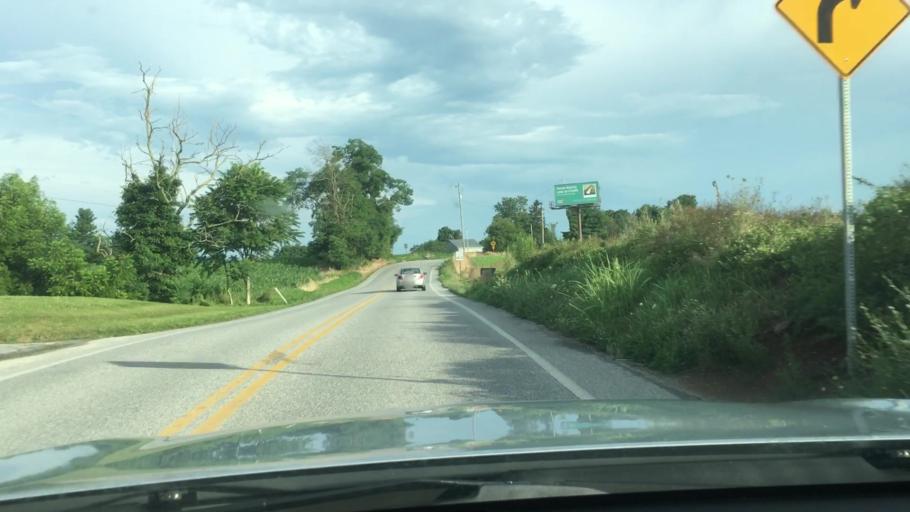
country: US
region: Pennsylvania
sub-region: York County
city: Weigelstown
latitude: 40.0077
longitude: -76.8043
